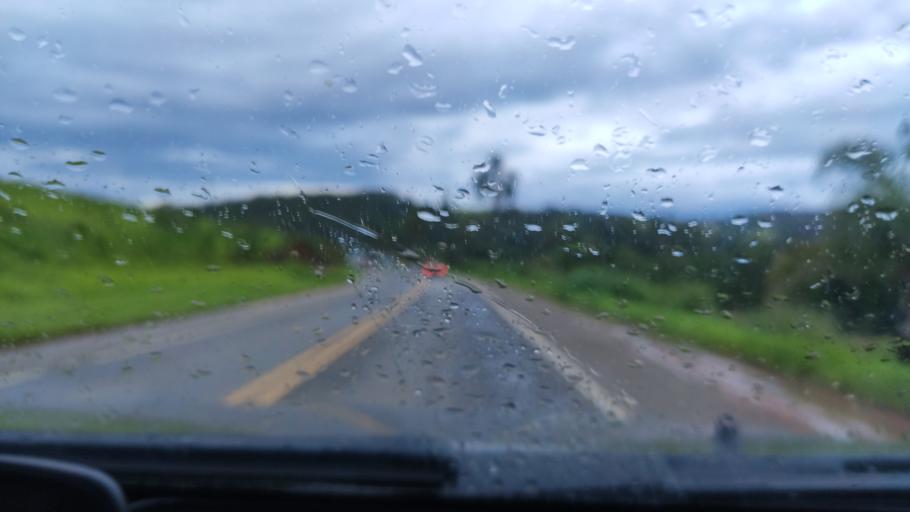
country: BR
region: Sao Paulo
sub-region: Braganca Paulista
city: Braganca Paulista
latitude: -22.7946
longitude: -46.5550
